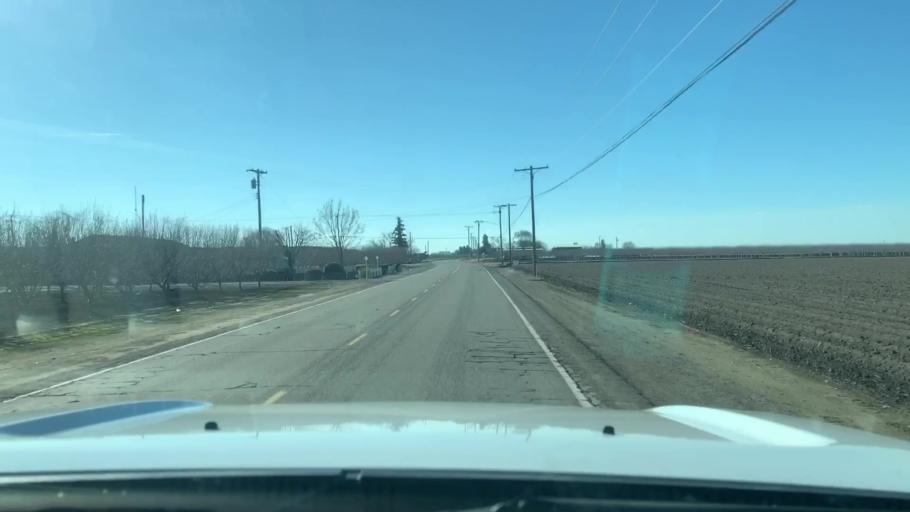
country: US
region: California
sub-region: Tulare County
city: Tulare
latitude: 36.1812
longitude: -119.4556
